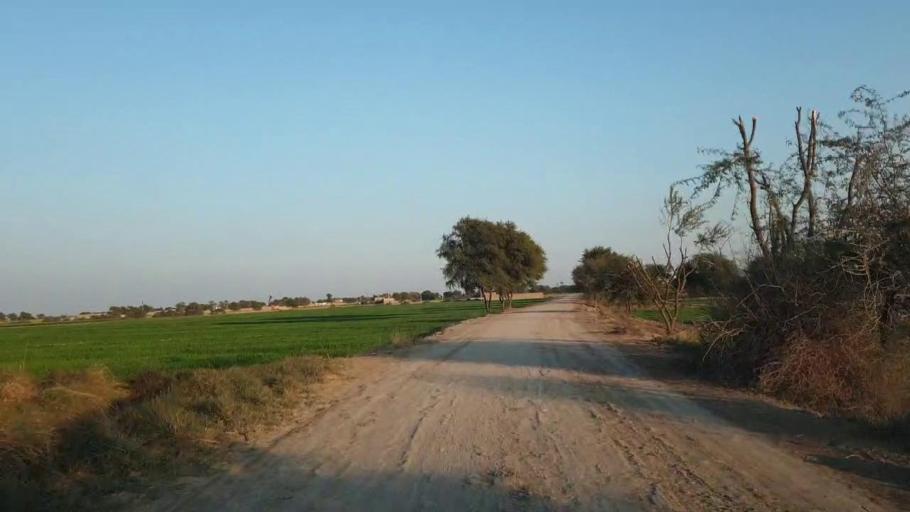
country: PK
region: Sindh
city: Shahpur Chakar
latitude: 26.1525
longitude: 68.5615
